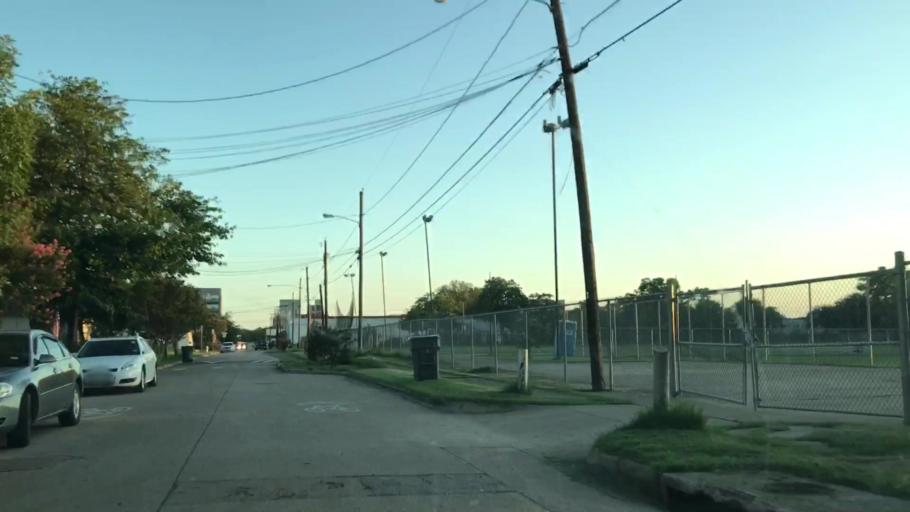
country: US
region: Texas
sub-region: Dallas County
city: Dallas
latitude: 32.7815
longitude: -96.8302
